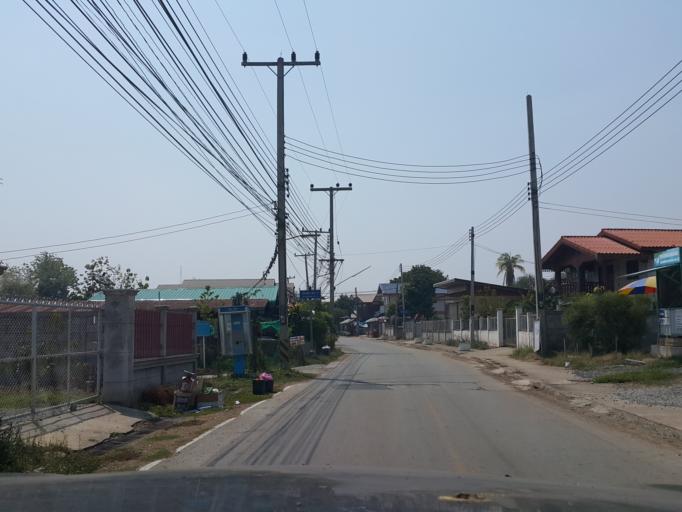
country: TH
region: Sukhothai
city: Thung Saliam
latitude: 17.3129
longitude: 99.5458
